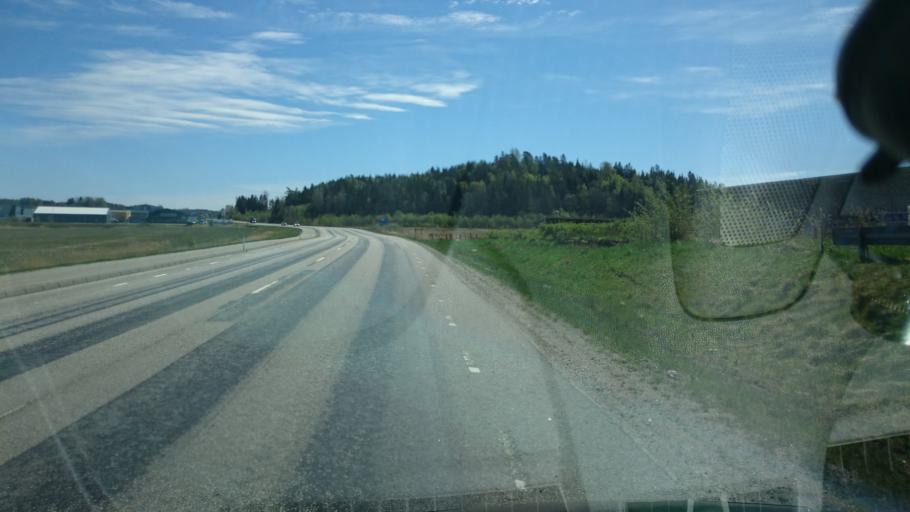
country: SE
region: Vaestra Goetaland
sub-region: Munkedals Kommun
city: Munkedal
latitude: 58.4820
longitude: 11.6377
